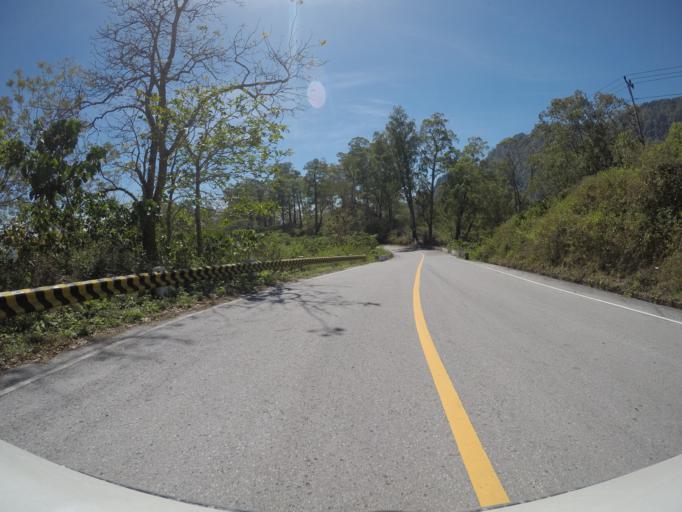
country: TL
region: Manufahi
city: Same
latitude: -8.8905
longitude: 125.9834
